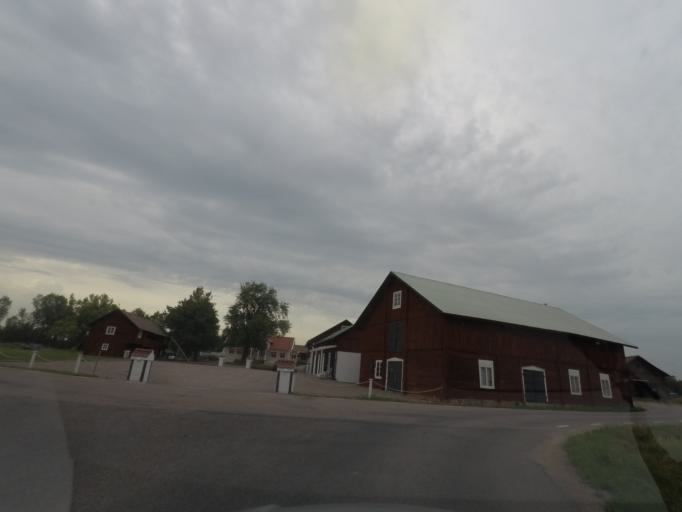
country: SE
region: Vaestmanland
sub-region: Hallstahammars Kommun
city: Kolback
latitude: 59.5141
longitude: 16.1863
